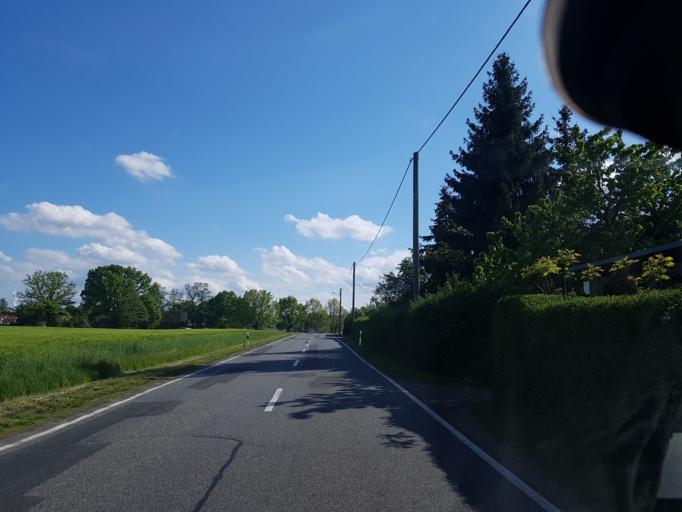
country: DE
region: Brandenburg
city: Drebkau
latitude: 51.6408
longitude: 14.2779
